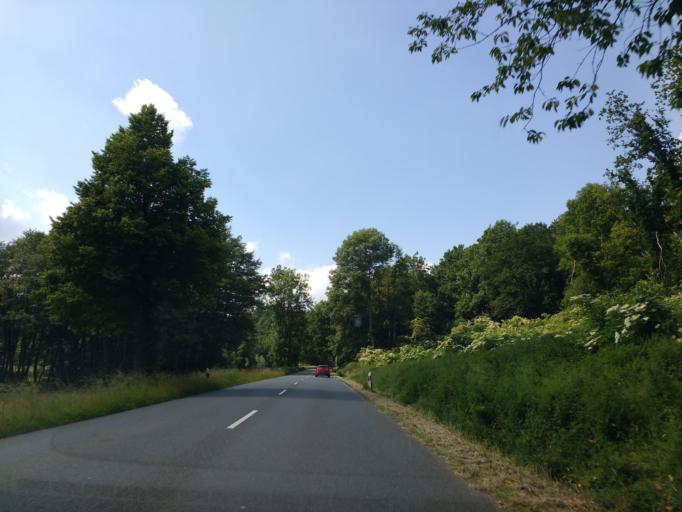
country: DE
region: North Rhine-Westphalia
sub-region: Regierungsbezirk Detmold
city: Dorentrup
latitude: 52.1168
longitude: 8.9506
